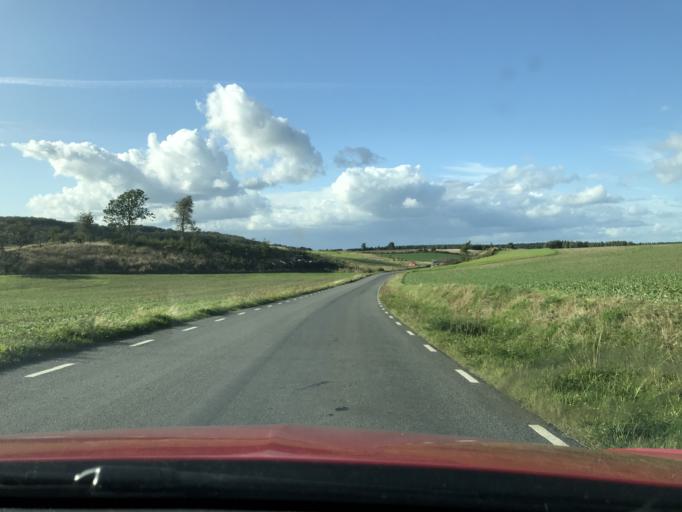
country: SE
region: Skane
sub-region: Kristianstads Kommun
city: Degeberga
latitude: 55.8423
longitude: 14.0859
